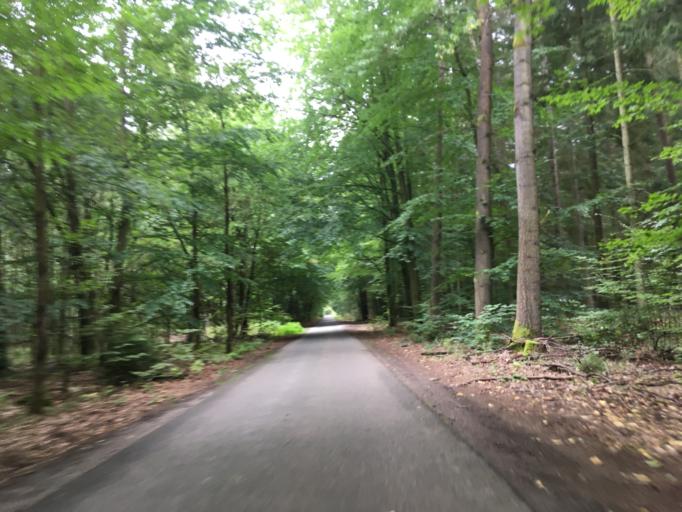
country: DE
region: Brandenburg
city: Gransee
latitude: 53.0665
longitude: 13.1898
